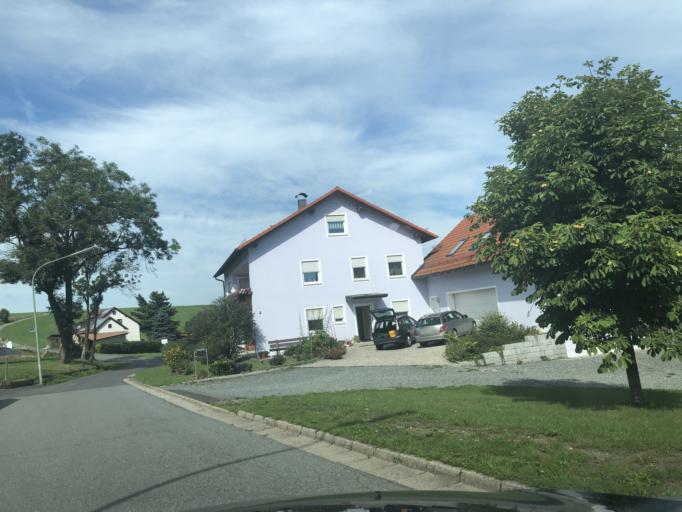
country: DE
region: Bavaria
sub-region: Upper Palatinate
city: Trabitz
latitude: 49.7802
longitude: 11.8979
